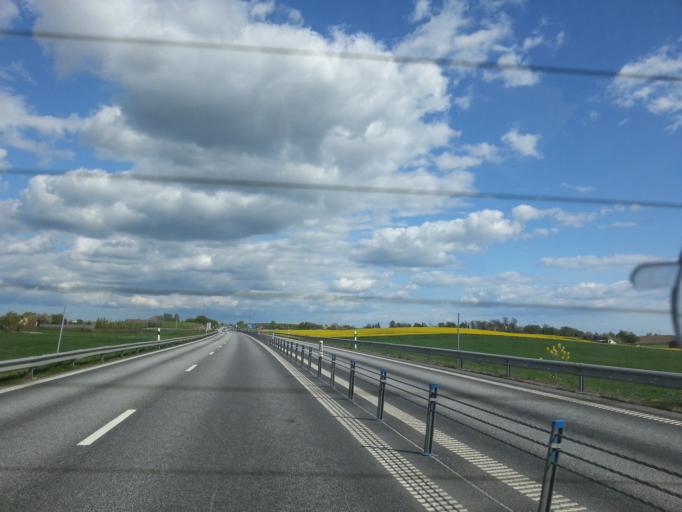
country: SE
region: Skane
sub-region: Skurups Kommun
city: Rydsgard
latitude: 55.4832
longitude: 13.5866
